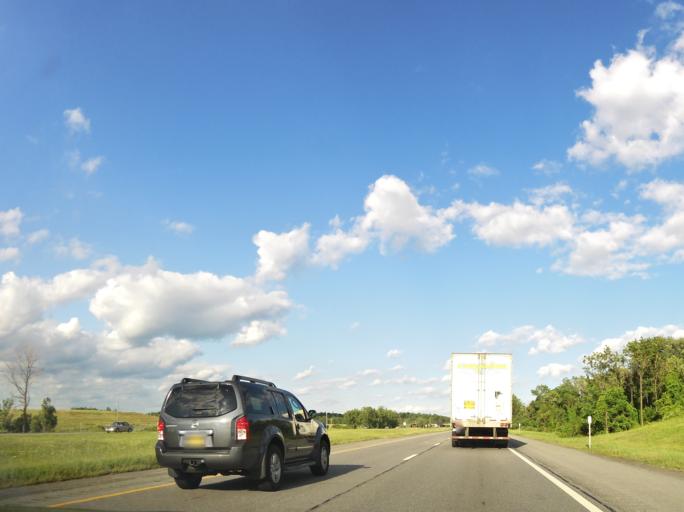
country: US
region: New York
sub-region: Genesee County
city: Oakfield
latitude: 43.0163
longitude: -78.2605
